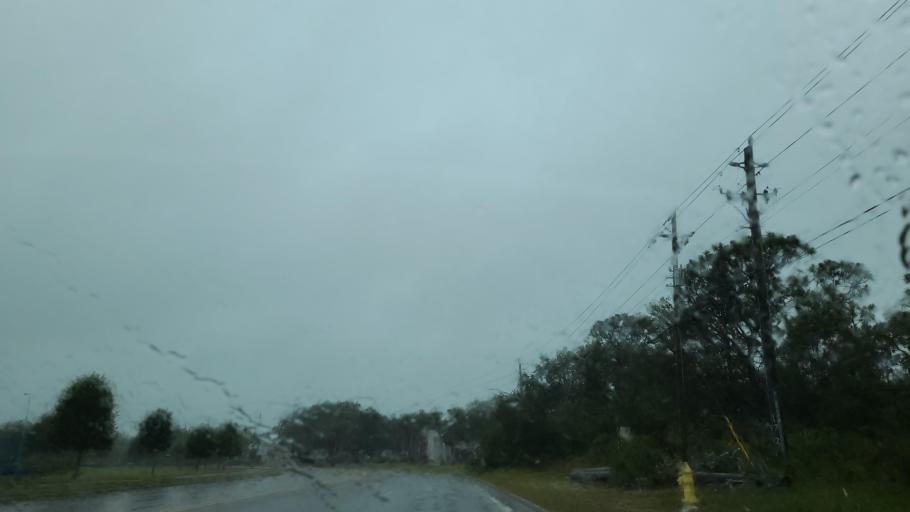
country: US
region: Florida
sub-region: Brevard County
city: West Melbourne
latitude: 28.0902
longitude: -80.6516
